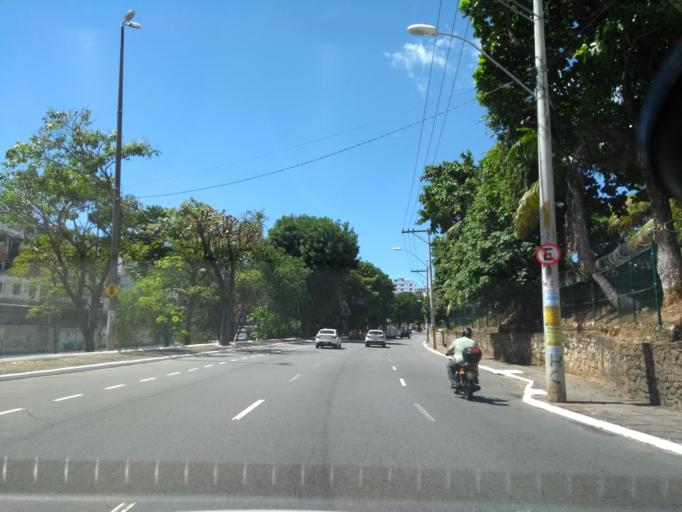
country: BR
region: Bahia
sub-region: Salvador
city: Salvador
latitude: -12.9912
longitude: -38.5122
